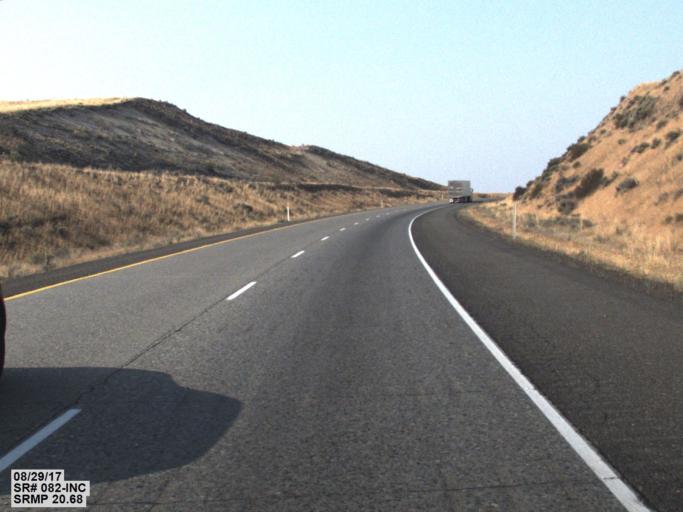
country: US
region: Washington
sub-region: Yakima County
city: Terrace Heights
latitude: 46.7272
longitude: -120.3903
